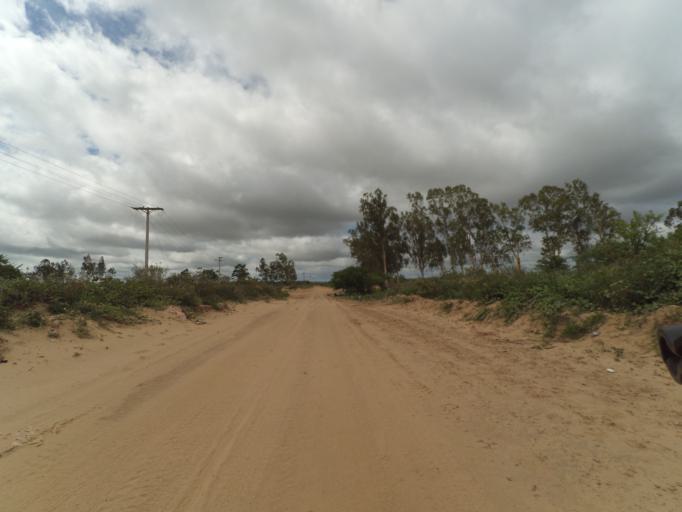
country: BO
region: Santa Cruz
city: Santa Cruz de la Sierra
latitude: -17.8846
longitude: -63.2378
